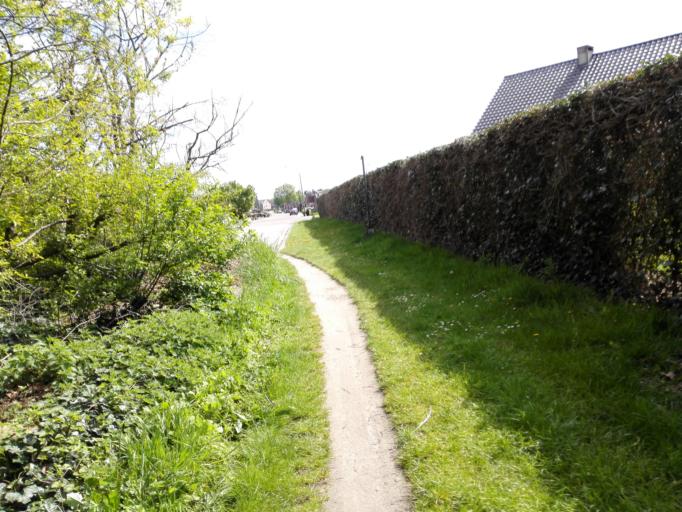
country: BE
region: Flanders
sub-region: Provincie Vlaams-Brabant
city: Rotselaar
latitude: 50.9523
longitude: 4.7225
